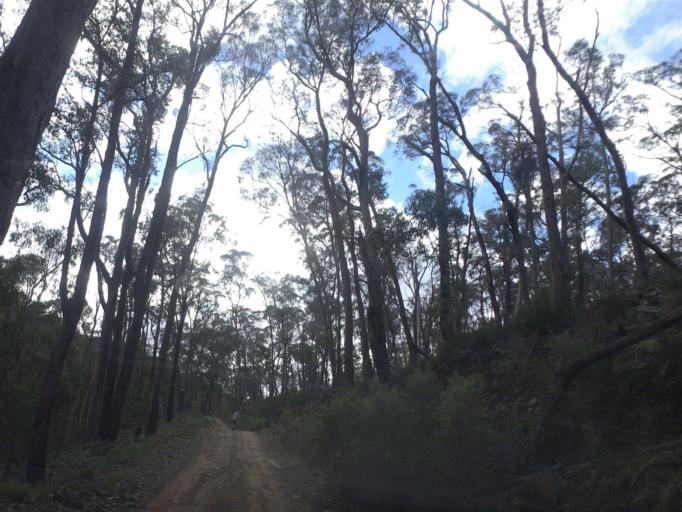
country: AU
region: Victoria
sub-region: Moorabool
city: Bacchus Marsh
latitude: -37.4630
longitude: 144.3112
